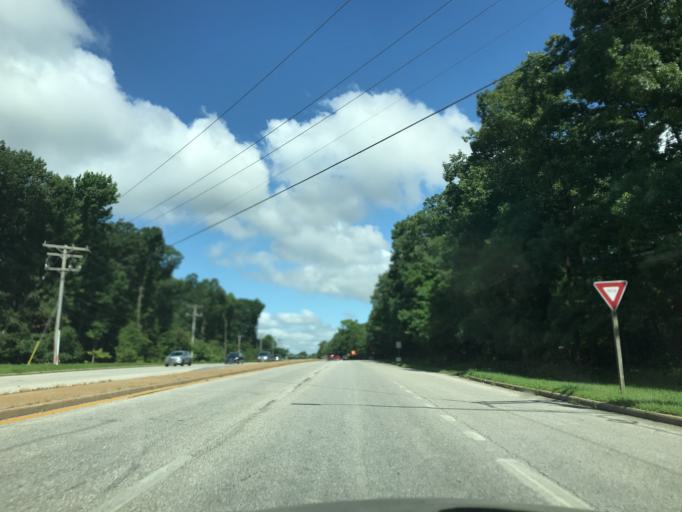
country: US
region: Maryland
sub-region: Anne Arundel County
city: Riviera Beach
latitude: 39.1779
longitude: -76.5427
